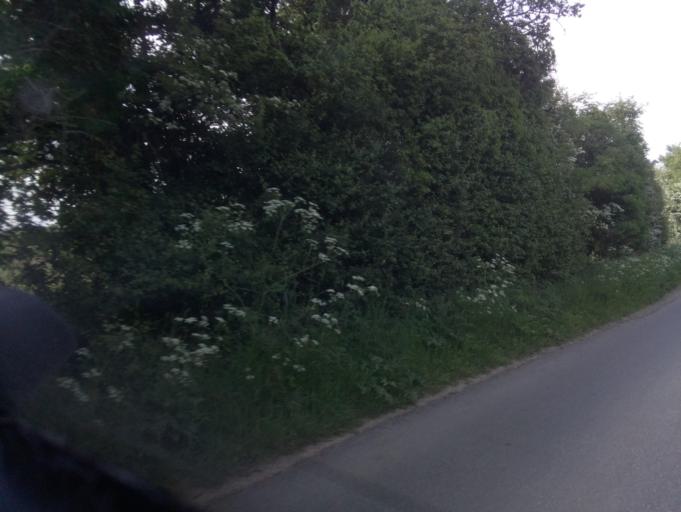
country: GB
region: England
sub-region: Gloucestershire
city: Westfield
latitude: 51.9282
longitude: -1.8332
